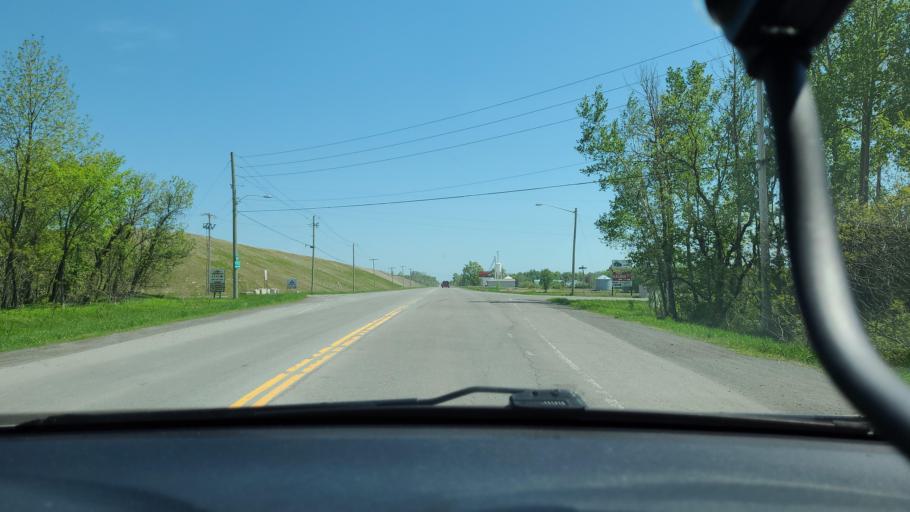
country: CA
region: Quebec
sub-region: Laurentides
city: Saint-Colomban
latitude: 45.6665
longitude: -74.1723
